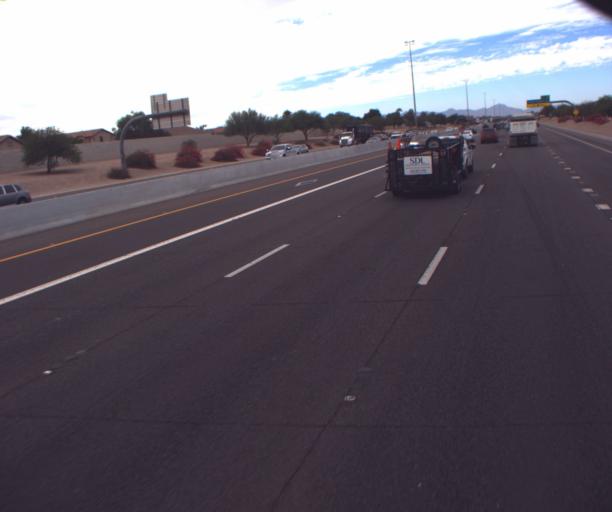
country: US
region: Arizona
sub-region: Maricopa County
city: Chandler
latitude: 33.2874
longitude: -111.8463
